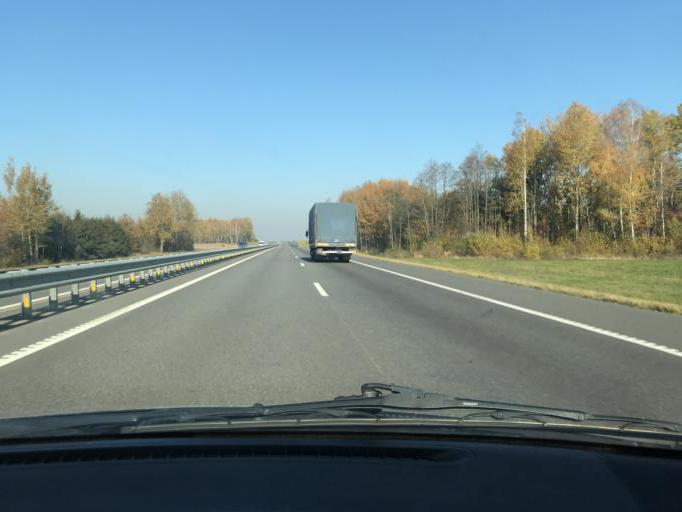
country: BY
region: Minsk
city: Slutsk
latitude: 53.1976
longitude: 27.5511
